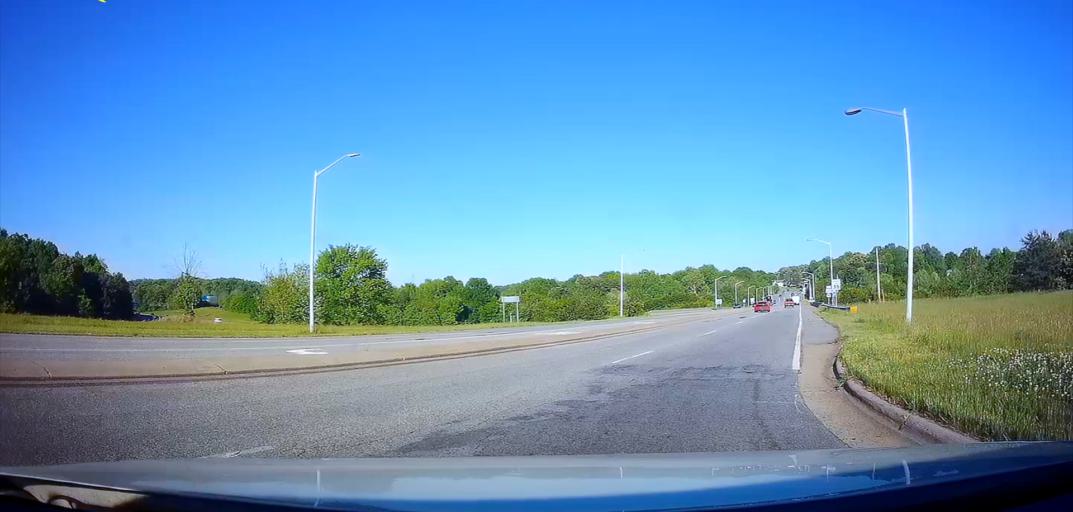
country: US
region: North Carolina
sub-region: Guilford County
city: Greensboro
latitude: 36.0281
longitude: -79.8250
